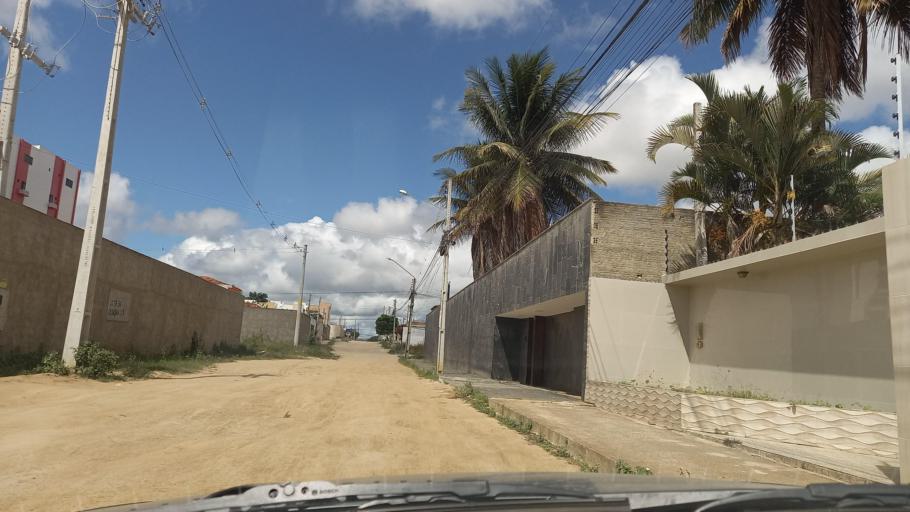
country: BR
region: Pernambuco
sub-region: Caruaru
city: Caruaru
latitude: -8.2565
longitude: -35.9793
